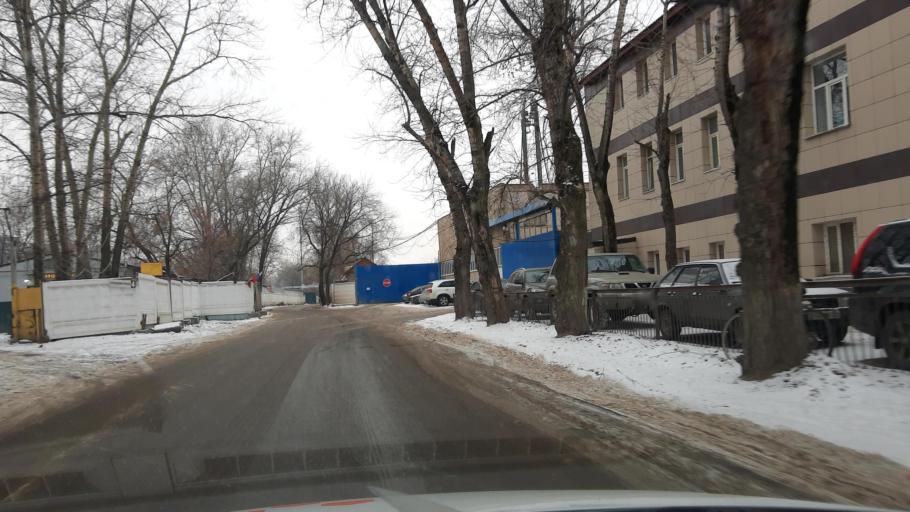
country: RU
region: Moscow
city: Lyublino
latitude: 55.6713
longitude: 37.7346
